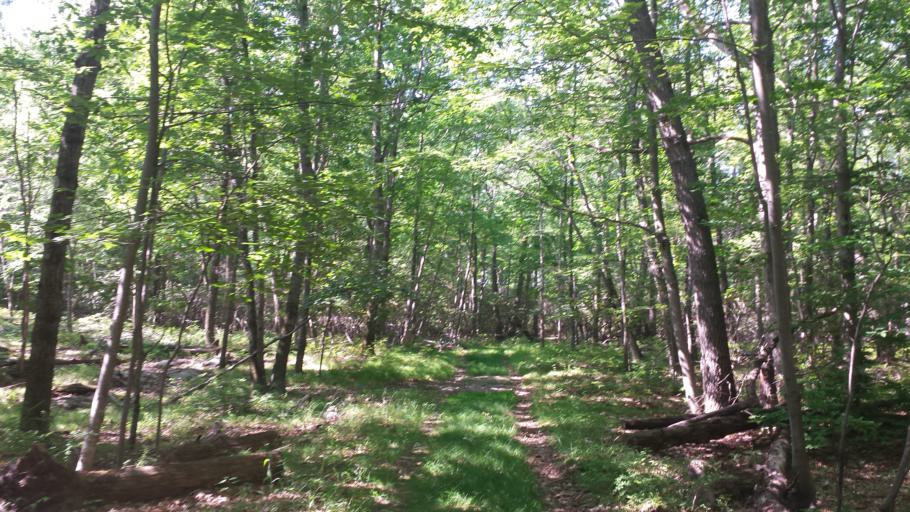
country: US
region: New York
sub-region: Westchester County
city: Pound Ridge
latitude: 41.2493
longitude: -73.5753
